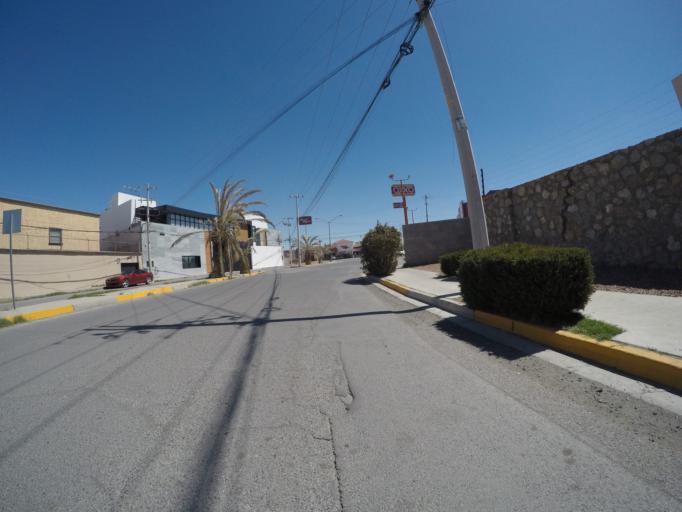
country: MX
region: Chihuahua
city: Ciudad Juarez
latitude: 31.6922
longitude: -106.4202
